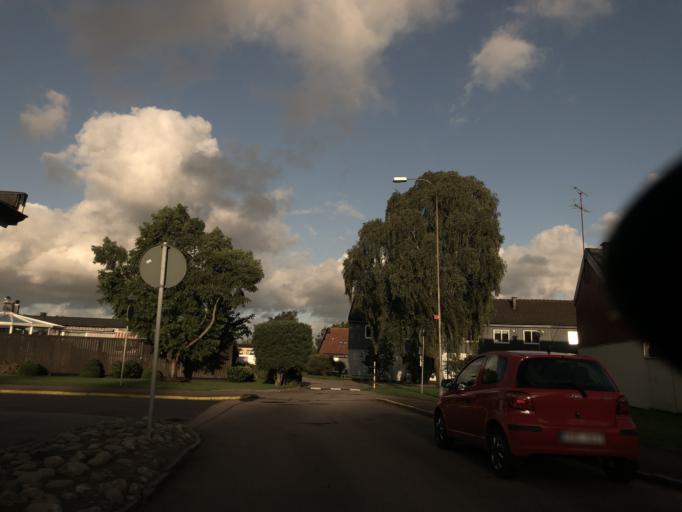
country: SE
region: Vaestra Goetaland
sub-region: Goteborg
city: Goeteborg
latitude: 57.7615
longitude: 11.9237
